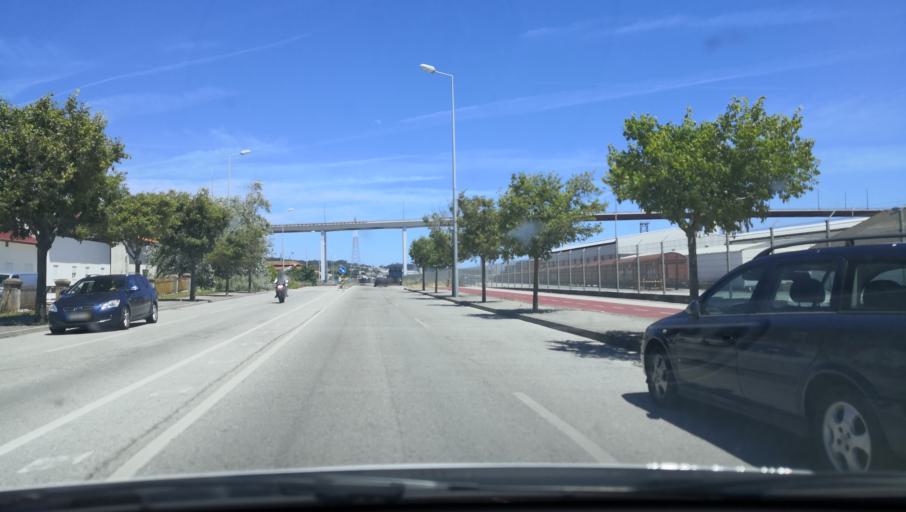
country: PT
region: Coimbra
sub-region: Figueira da Foz
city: Figueira da Foz
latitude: 40.1480
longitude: -8.8467
